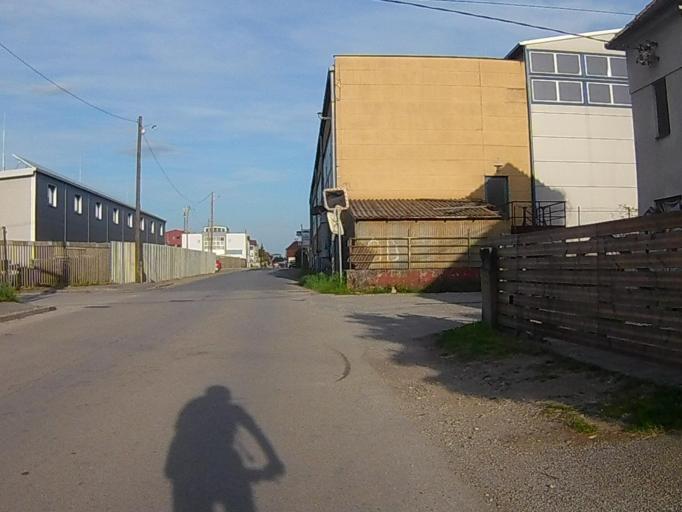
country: SI
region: Maribor
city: Kamnica
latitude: 46.5588
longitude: 15.6171
